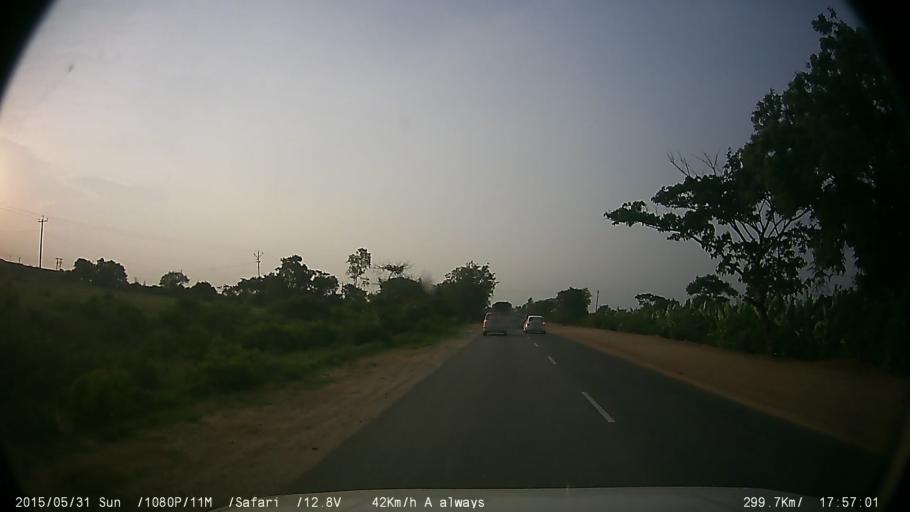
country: IN
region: Karnataka
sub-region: Mysore
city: Nanjangud
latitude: 11.9980
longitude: 76.6694
